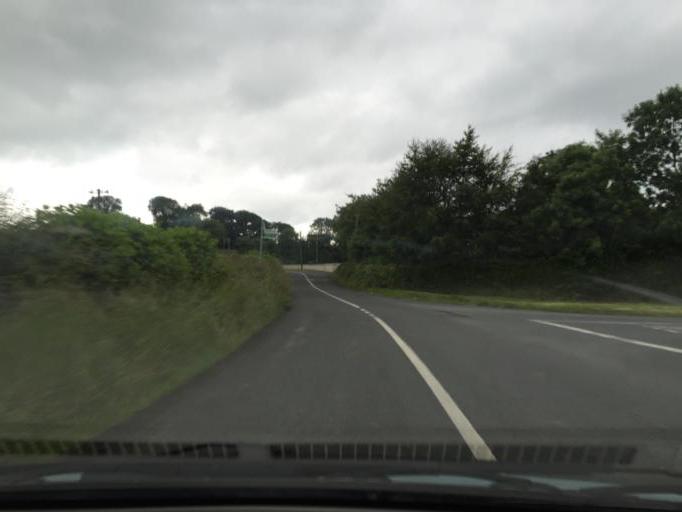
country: IE
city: Ballisodare
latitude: 54.2629
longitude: -8.5248
